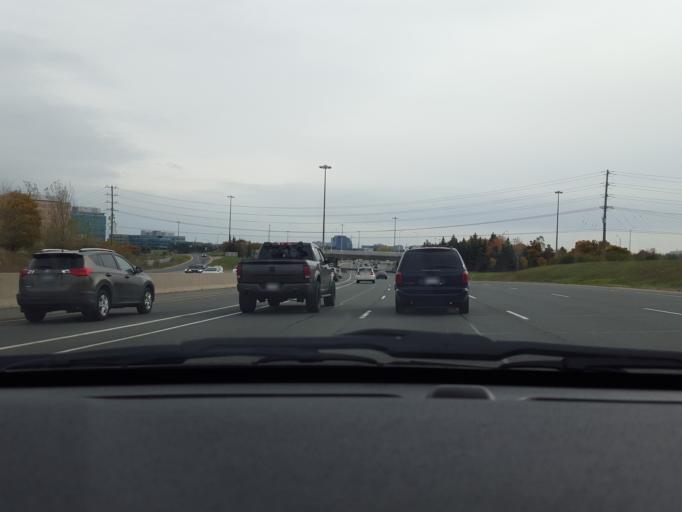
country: CA
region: Ontario
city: Willowdale
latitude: 43.8146
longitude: -79.3561
